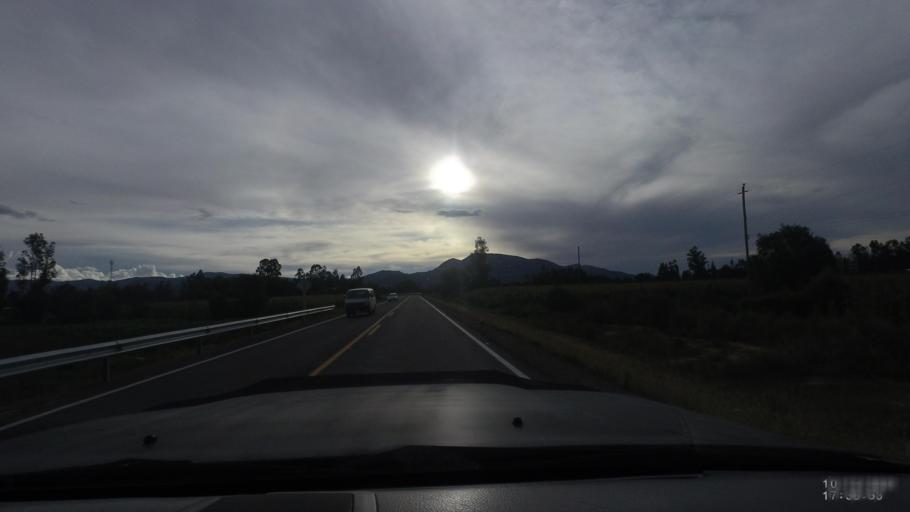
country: BO
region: Cochabamba
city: Tarata
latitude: -17.5746
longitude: -66.0107
